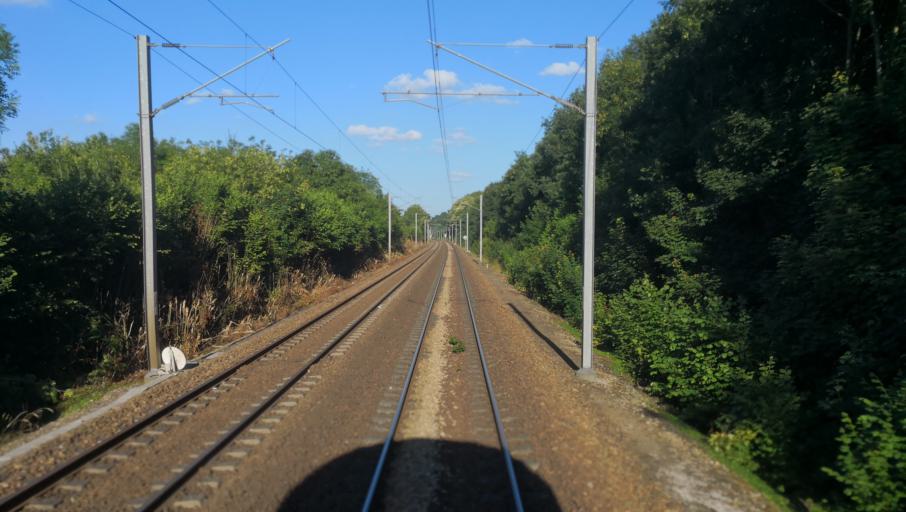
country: FR
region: Ile-de-France
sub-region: Departement des Yvelines
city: Rosny-sur-Seine
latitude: 48.9837
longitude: 1.6362
